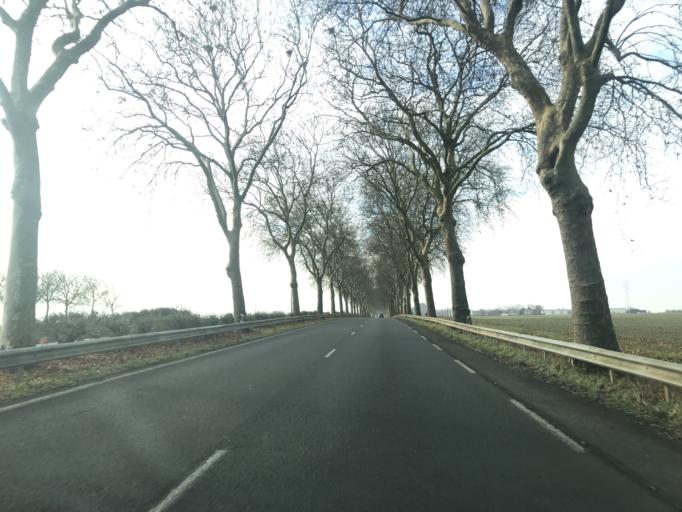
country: FR
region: Poitou-Charentes
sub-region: Departement des Deux-Sevres
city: Chauray
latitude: 46.3470
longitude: -0.3594
